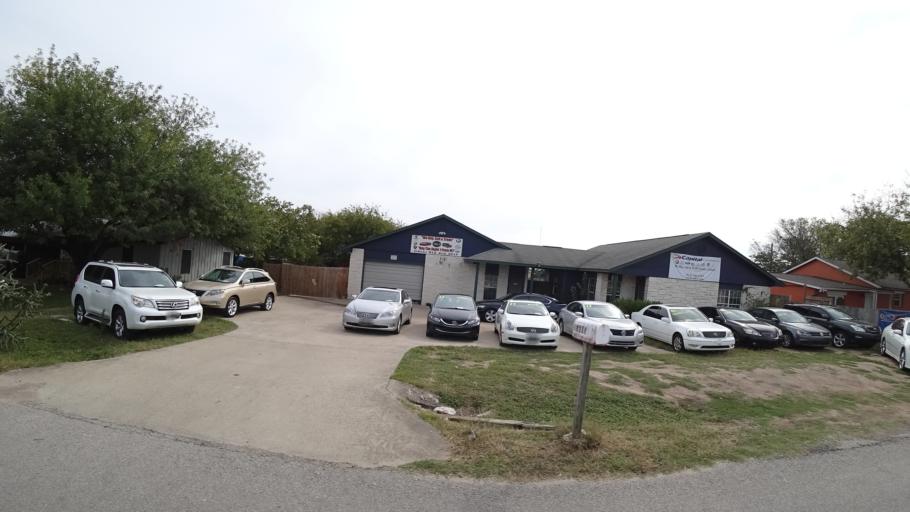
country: US
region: Texas
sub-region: Travis County
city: Wells Branch
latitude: 30.4530
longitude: -97.6676
